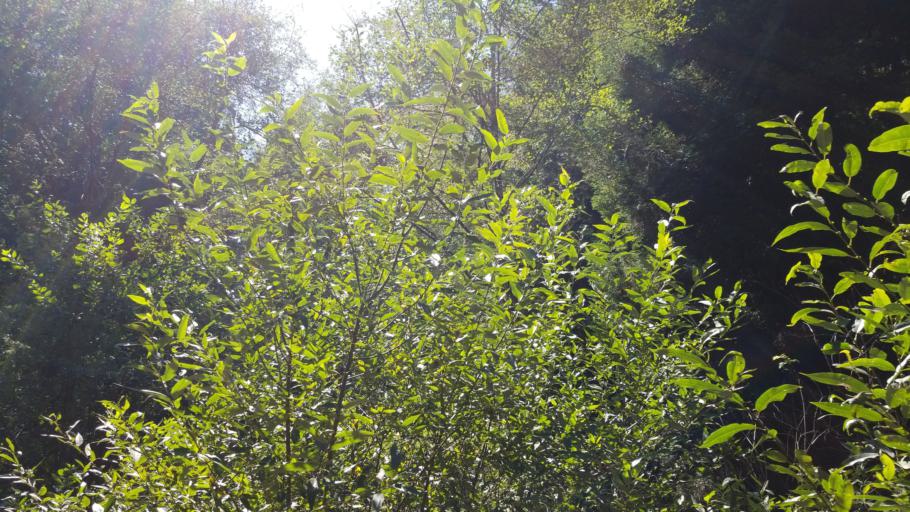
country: US
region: California
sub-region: Mendocino County
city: Fort Bragg
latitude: 39.4492
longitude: -123.7760
